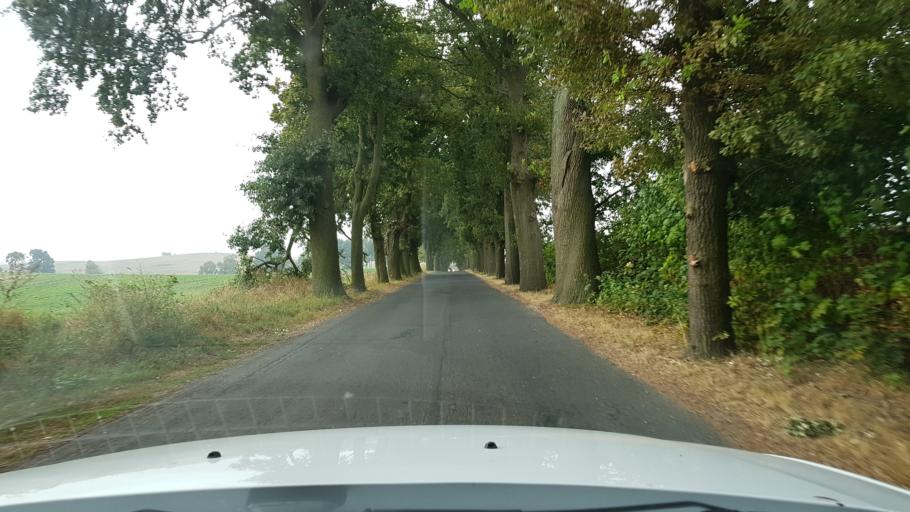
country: PL
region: West Pomeranian Voivodeship
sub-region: Powiat gryfinski
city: Moryn
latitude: 52.8913
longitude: 14.3782
